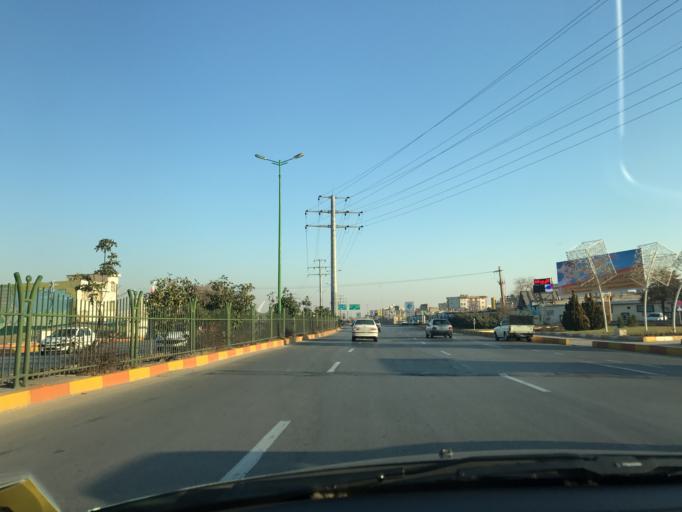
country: IR
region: Qazvin
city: Qazvin
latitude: 36.2871
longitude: 50.0109
